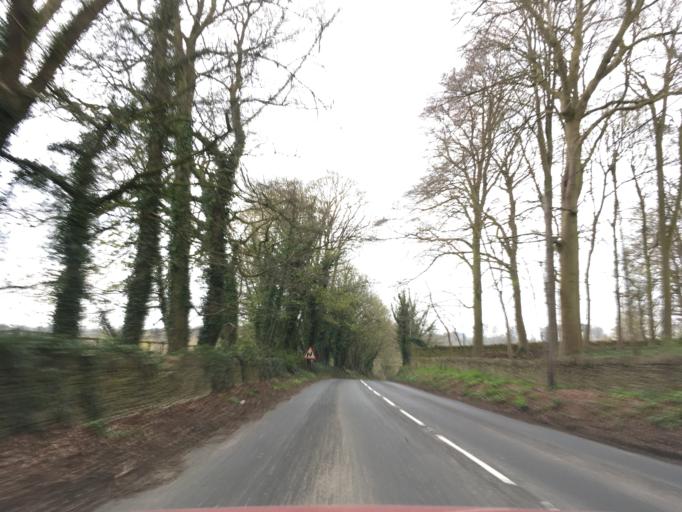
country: GB
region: England
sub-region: Gloucestershire
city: Northleach
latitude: 51.7613
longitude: -1.8280
